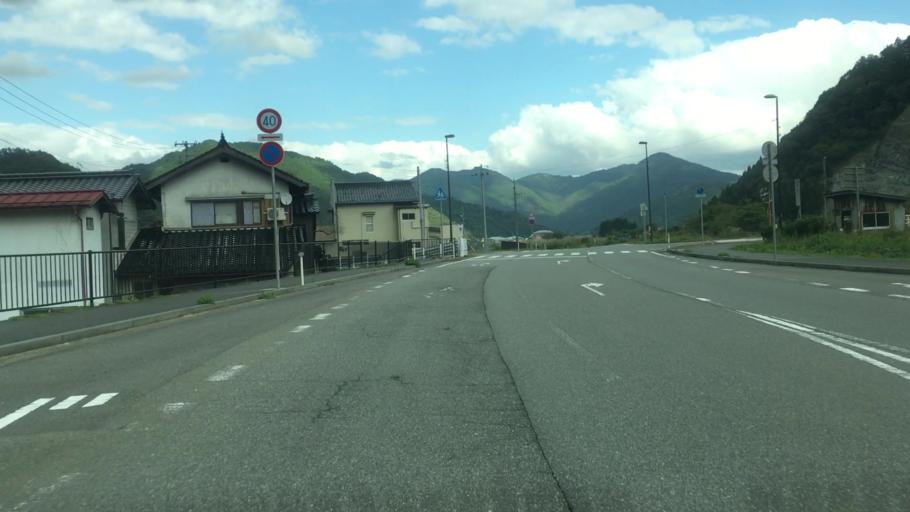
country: JP
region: Hyogo
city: Toyooka
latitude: 35.3715
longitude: 134.7639
